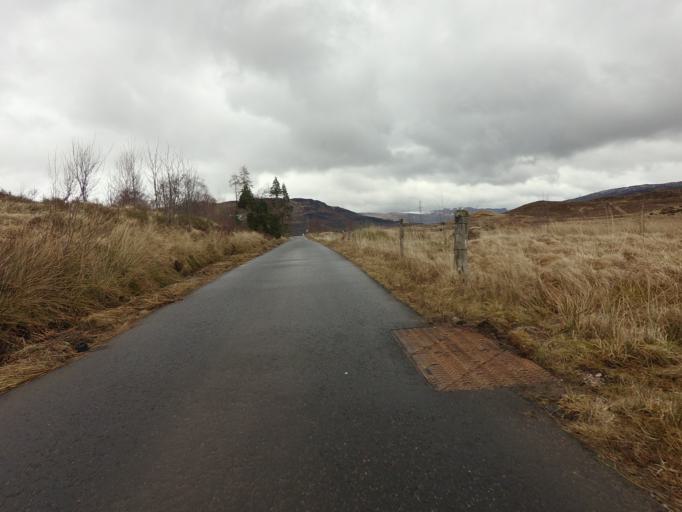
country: GB
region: Scotland
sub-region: West Dunbartonshire
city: Balloch
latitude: 56.2533
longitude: -4.5925
